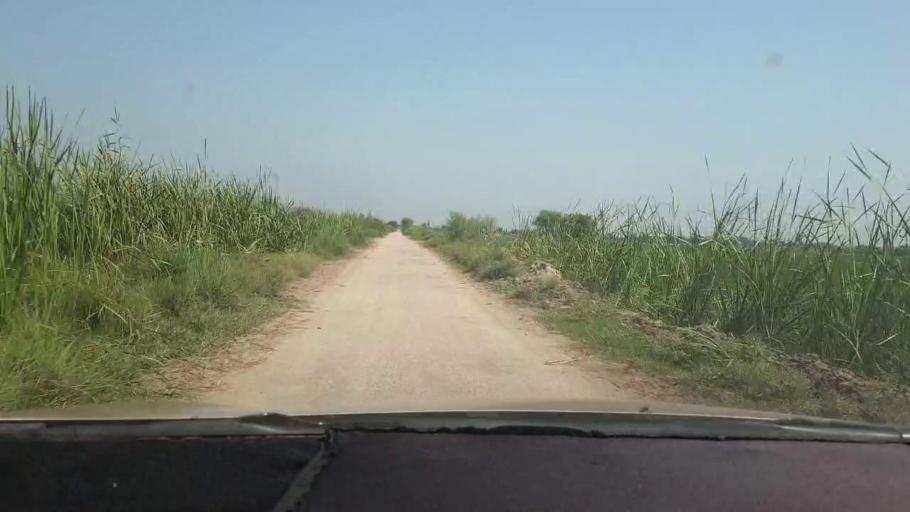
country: PK
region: Sindh
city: Miro Khan
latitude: 27.6977
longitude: 68.0941
